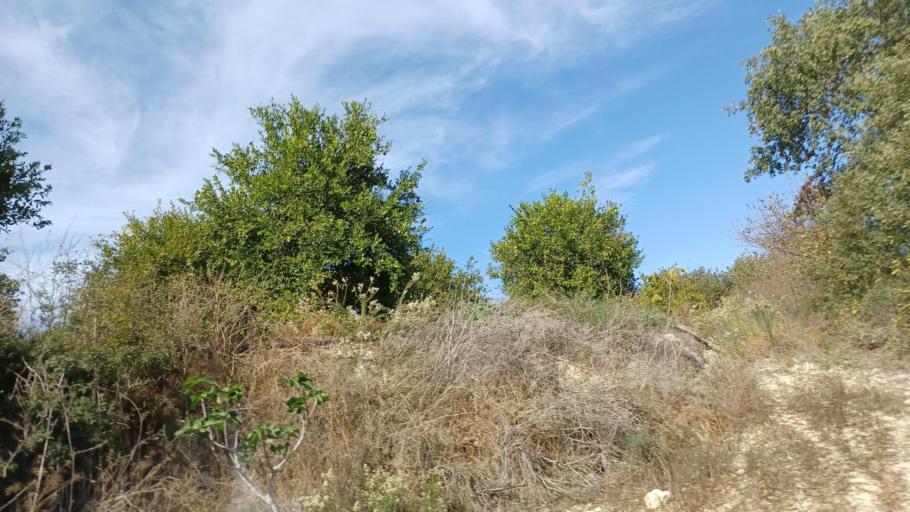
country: CY
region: Pafos
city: Pegeia
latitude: 34.9353
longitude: 32.4598
